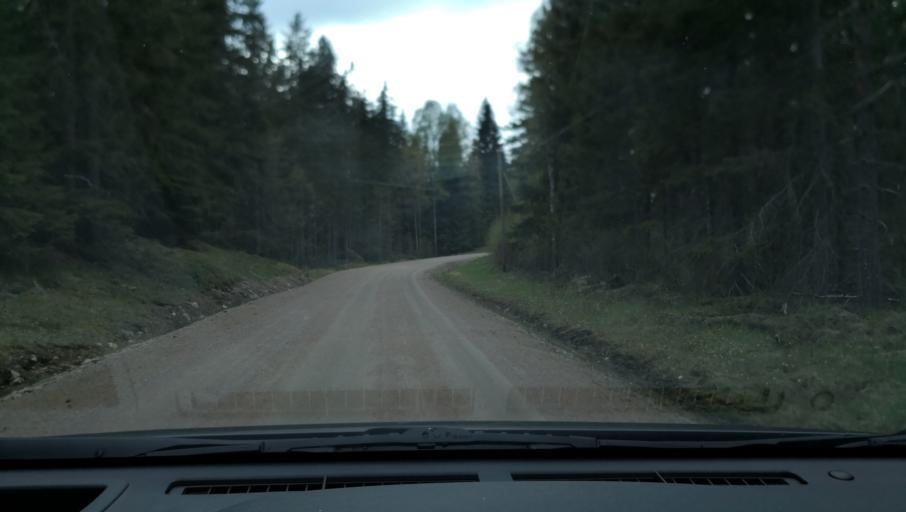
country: SE
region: Vaestmanland
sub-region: Fagersta Kommun
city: Fagersta
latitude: 60.1203
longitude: 15.7508
